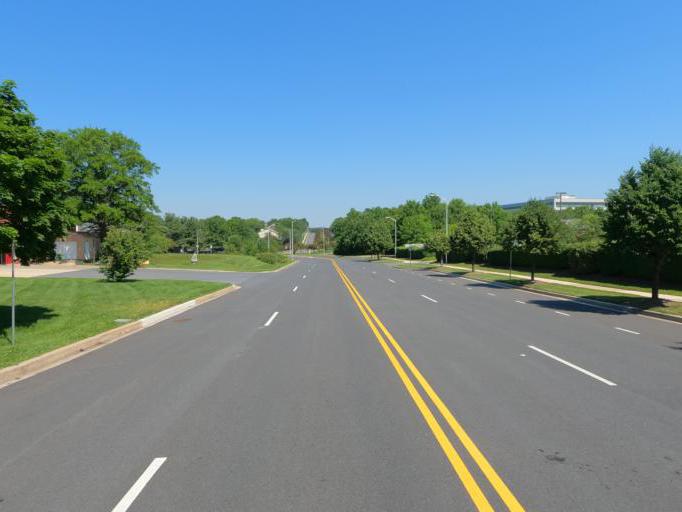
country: US
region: Maryland
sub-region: Montgomery County
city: Germantown
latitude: 39.1850
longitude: -77.2625
